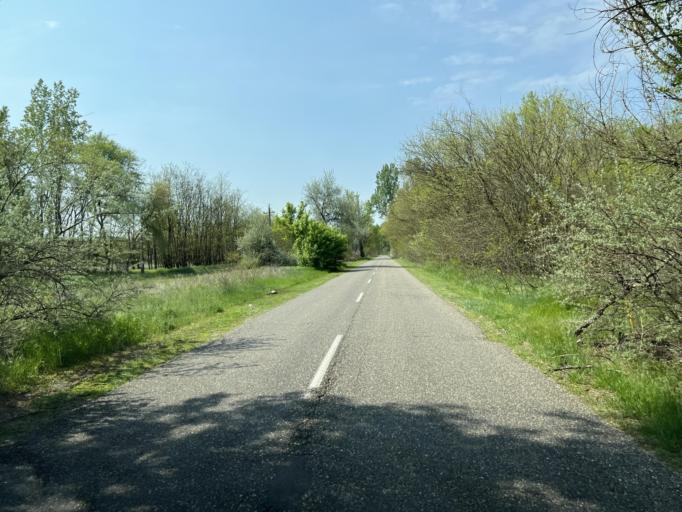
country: HU
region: Pest
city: Kocser
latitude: 47.0690
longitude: 19.8651
